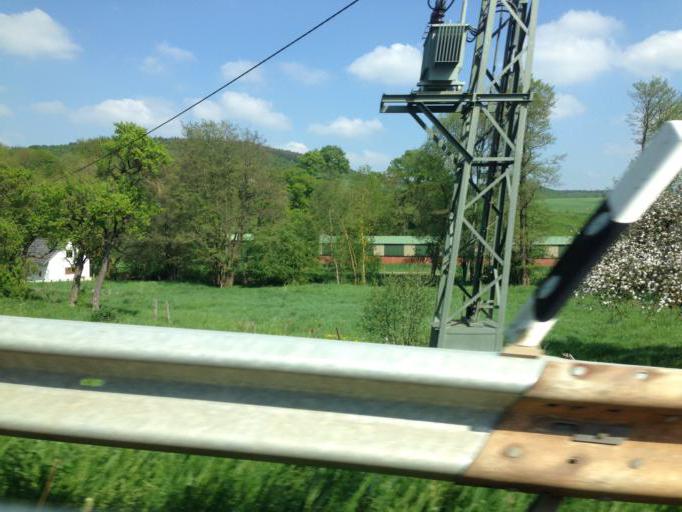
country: DE
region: North Rhine-Westphalia
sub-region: Regierungsbezirk Koln
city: Bad Munstereifel
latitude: 50.5548
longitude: 6.7199
